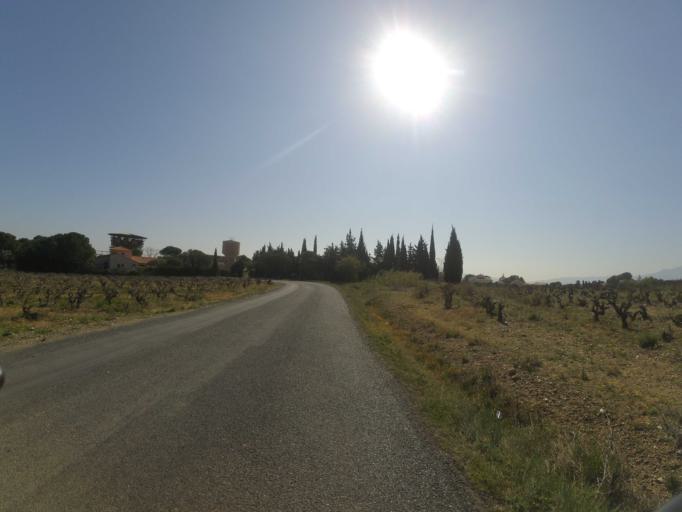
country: FR
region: Languedoc-Roussillon
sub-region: Departement des Pyrenees-Orientales
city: Llupia
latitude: 42.6097
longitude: 2.7673
